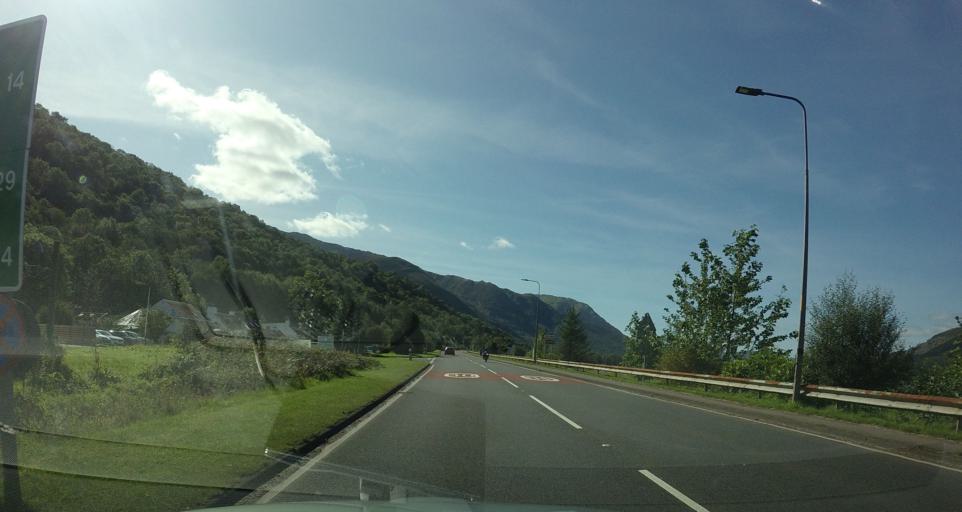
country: GB
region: Scotland
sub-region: Highland
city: Fort William
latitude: 56.6810
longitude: -5.1101
